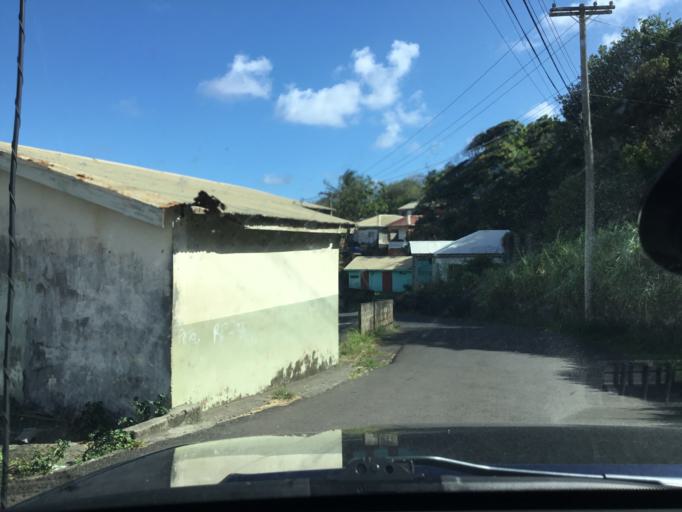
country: VC
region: Charlotte
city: Biabou
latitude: 13.1553
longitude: -61.1570
